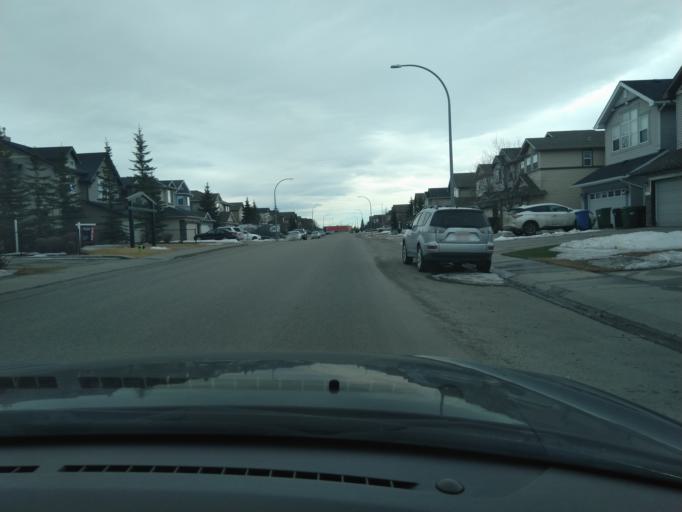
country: CA
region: Alberta
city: Calgary
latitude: 51.1598
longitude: -114.0868
